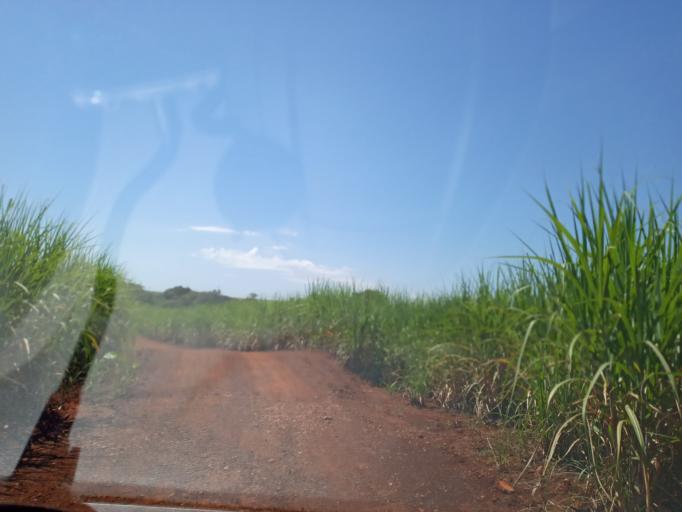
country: BR
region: Goias
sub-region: Itumbiara
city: Itumbiara
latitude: -18.4329
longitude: -49.1504
